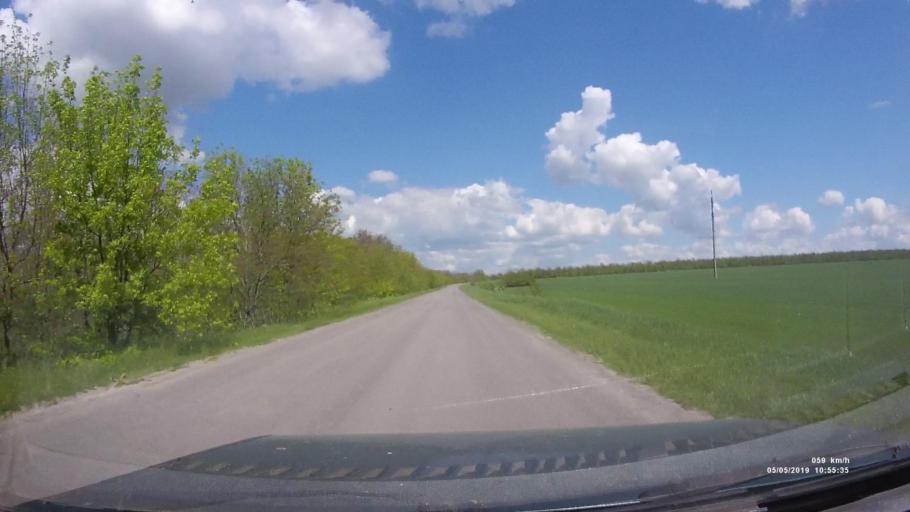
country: RU
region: Rostov
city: Ust'-Donetskiy
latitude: 47.6668
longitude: 40.8207
